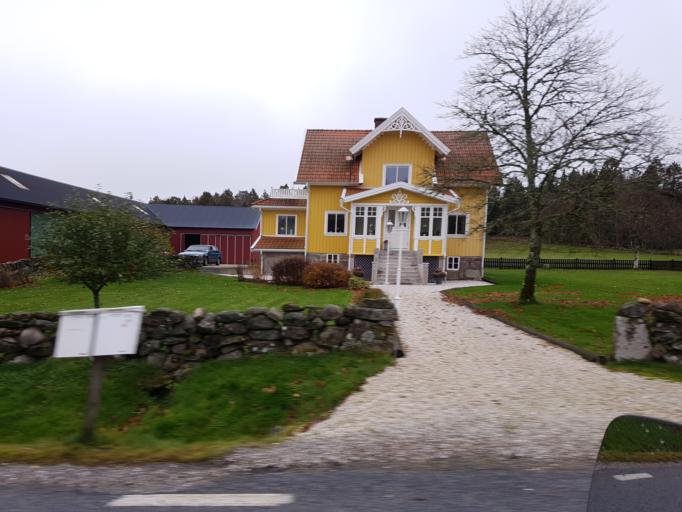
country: SE
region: Vaestra Goetaland
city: Svanesund
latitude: 58.1709
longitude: 11.7833
